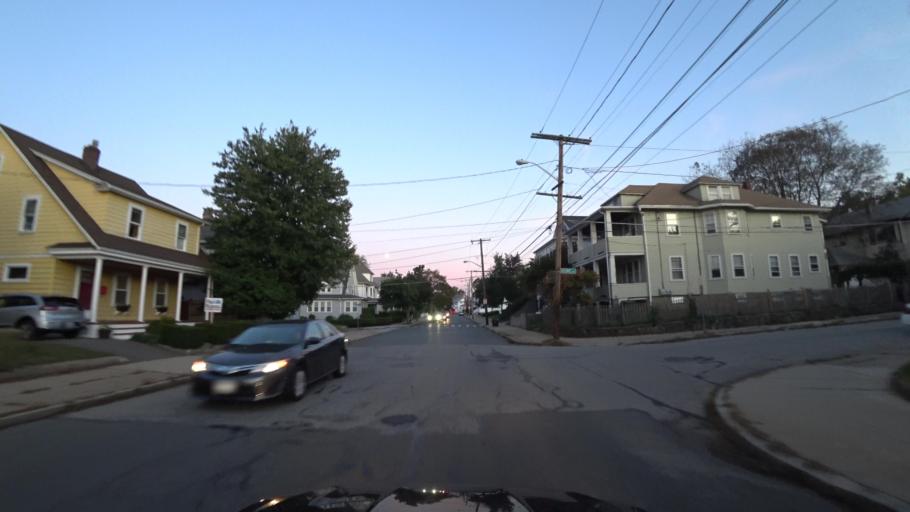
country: US
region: Massachusetts
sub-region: Middlesex County
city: Medford
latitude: 42.4128
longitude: -71.1162
